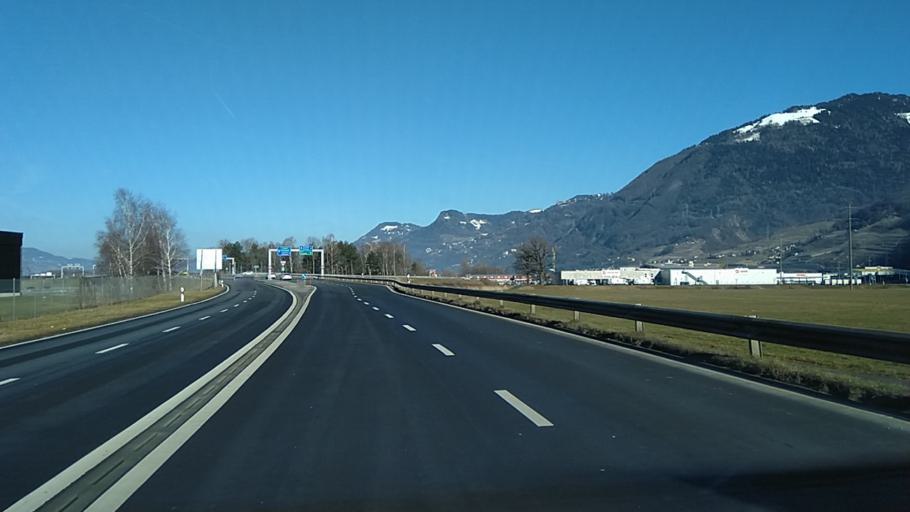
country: CH
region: Vaud
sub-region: Aigle District
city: Villeneuve
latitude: 46.3781
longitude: 6.9255
